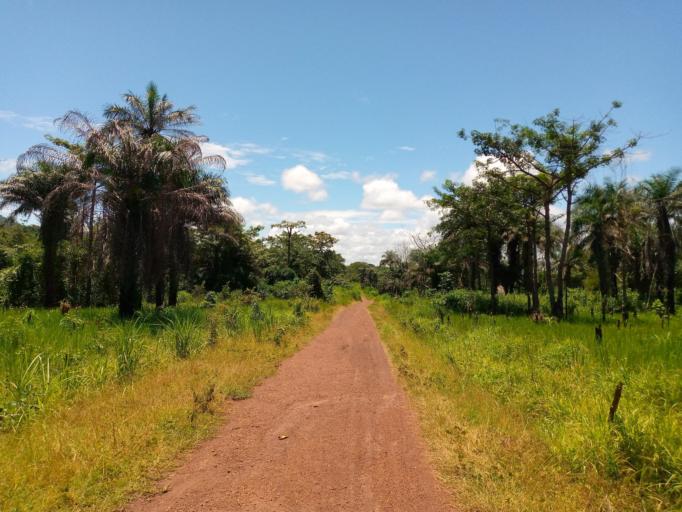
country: SL
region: Northern Province
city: Binkolo
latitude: 9.1068
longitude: -12.1393
